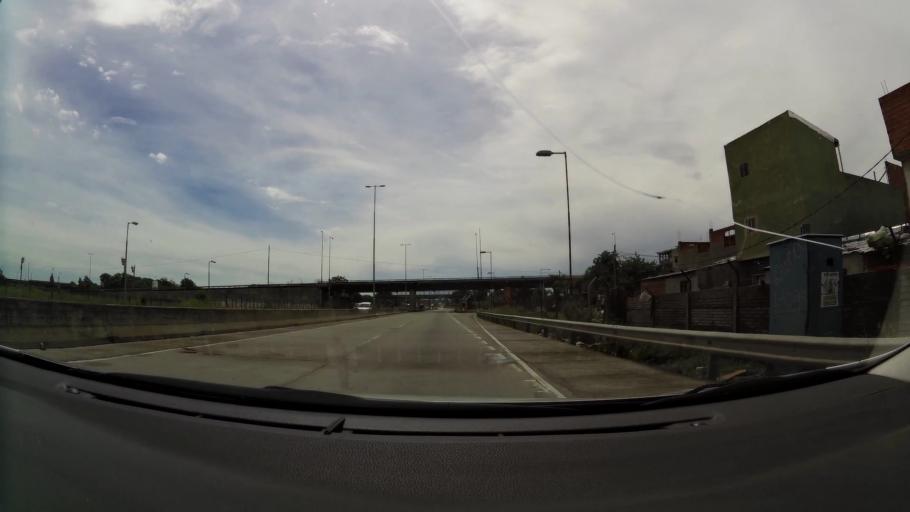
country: AR
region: Buenos Aires F.D.
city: Villa Lugano
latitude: -34.6574
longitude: -58.4595
